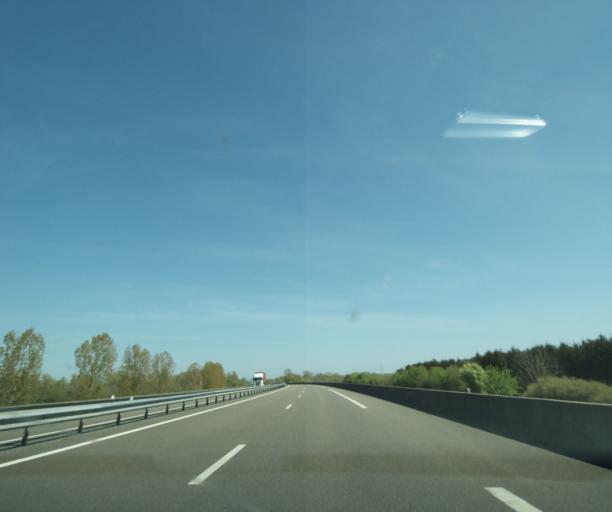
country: FR
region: Bourgogne
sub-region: Departement de la Nievre
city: Sermoise-sur-Loire
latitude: 46.9701
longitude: 3.1924
